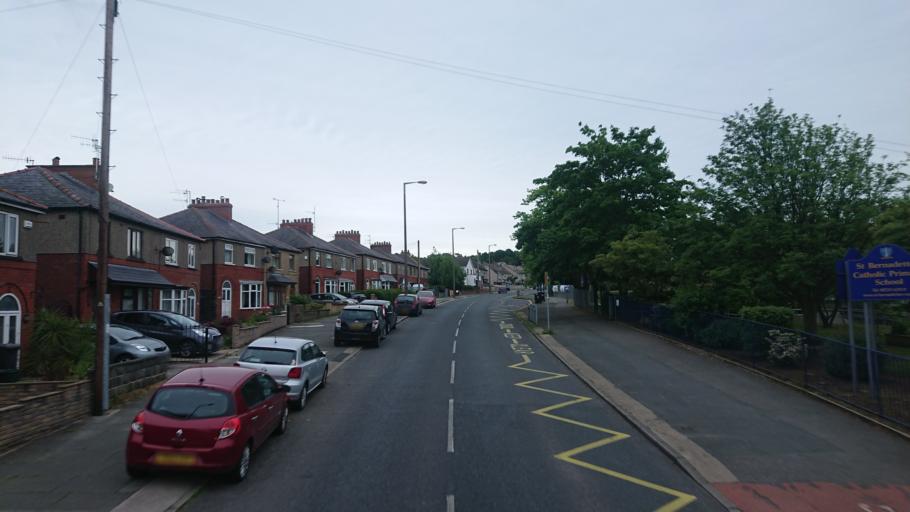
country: GB
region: England
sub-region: Lancashire
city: Lancaster
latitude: 54.0338
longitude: -2.7850
